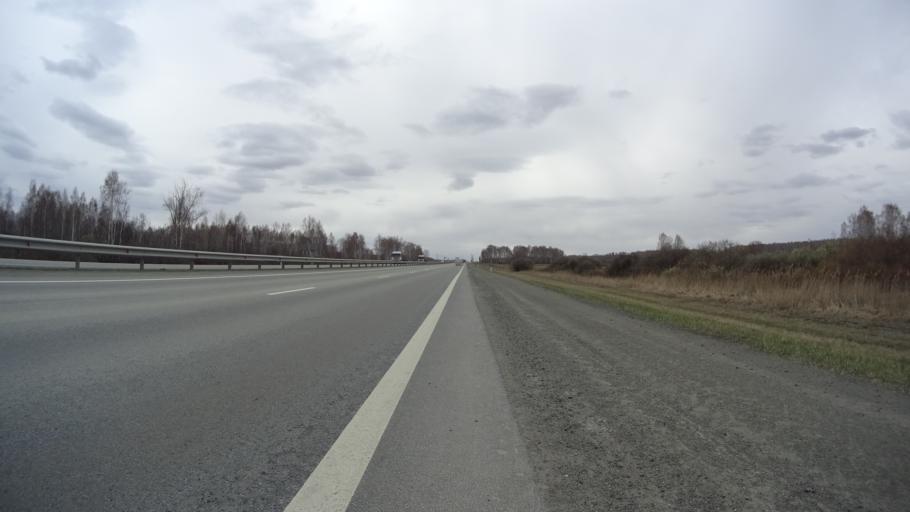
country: RU
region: Chelyabinsk
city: Yemanzhelinka
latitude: 54.8397
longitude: 61.3133
